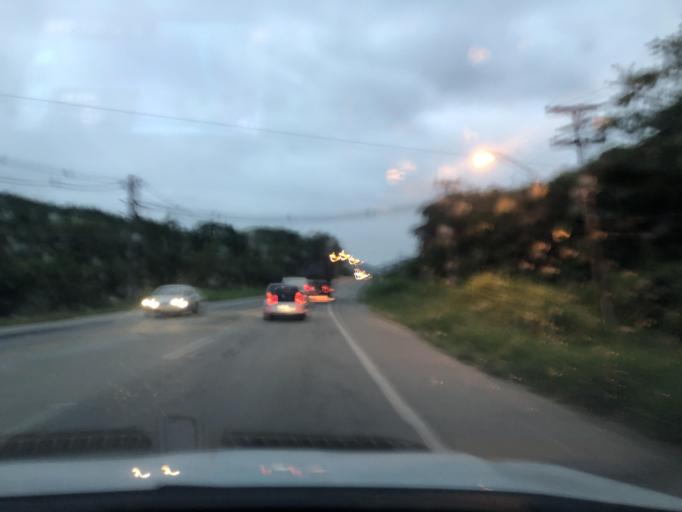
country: BR
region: Santa Catarina
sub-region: Pomerode
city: Pomerode
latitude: -26.7834
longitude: -49.0847
